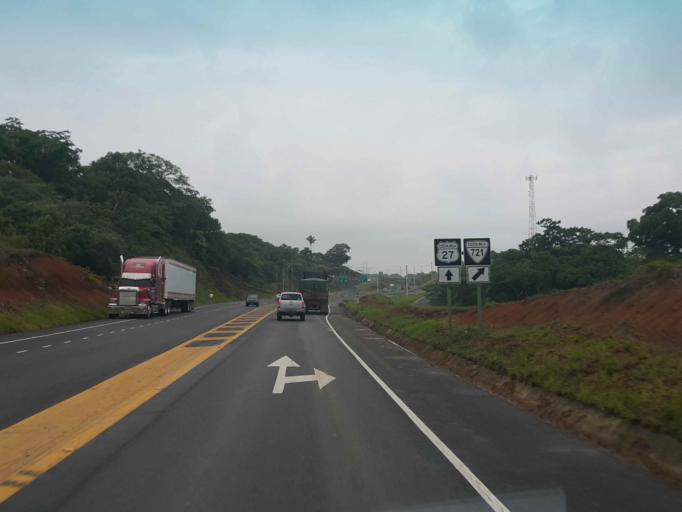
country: CR
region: Alajuela
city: Carrillos
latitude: 9.9647
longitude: -84.2859
